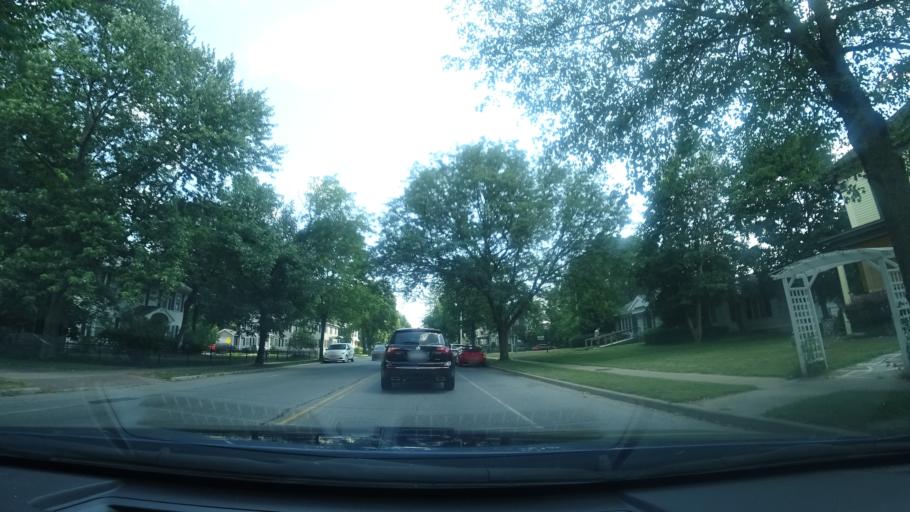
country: US
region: New York
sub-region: Warren County
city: Glens Falls
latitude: 43.3183
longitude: -73.6567
